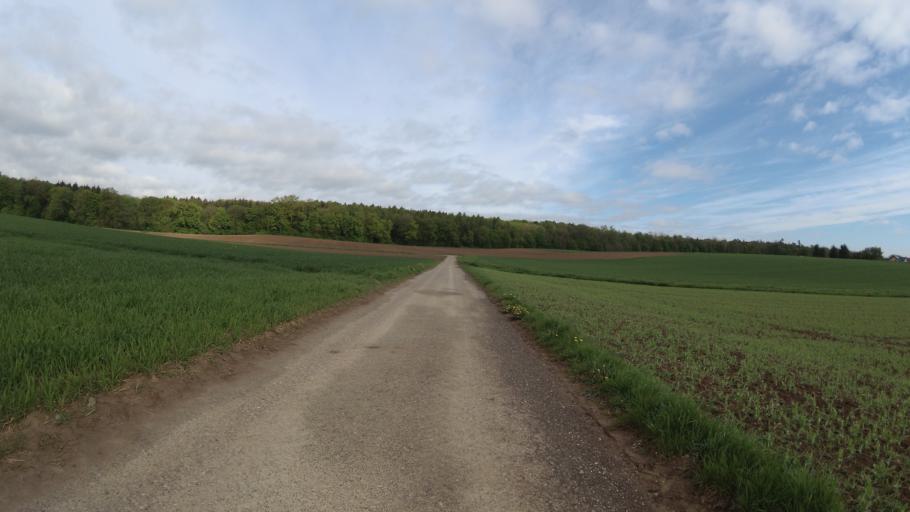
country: DE
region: Baden-Wuerttemberg
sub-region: Regierungsbezirk Stuttgart
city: Neuenstadt am Kocher
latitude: 49.2245
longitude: 9.2987
